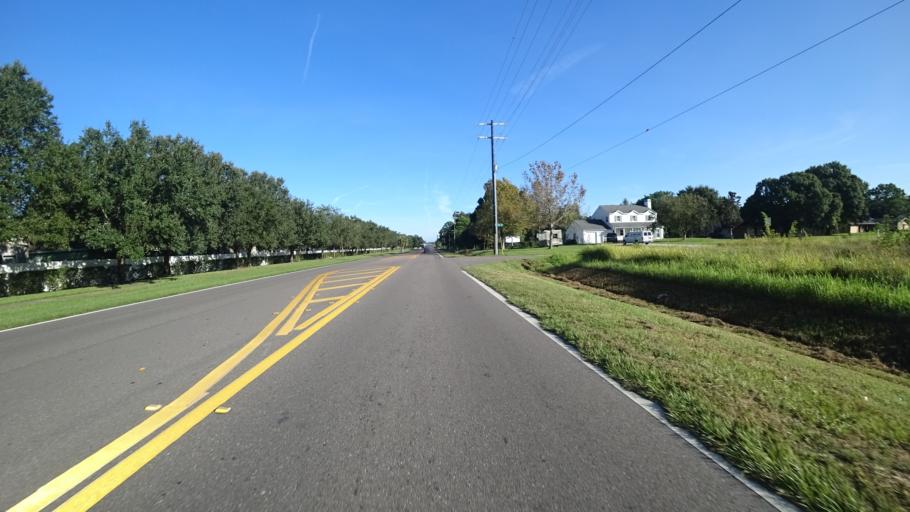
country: US
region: Florida
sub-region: Manatee County
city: Memphis
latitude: 27.5761
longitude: -82.5275
